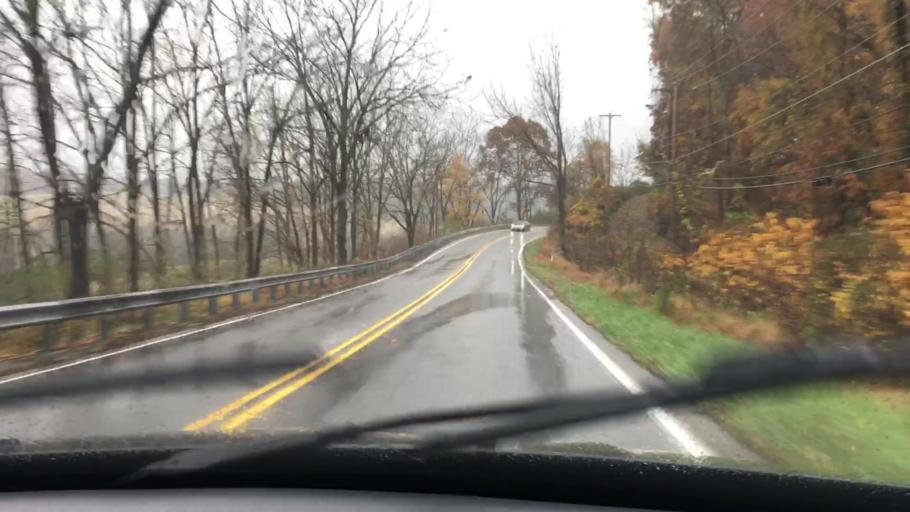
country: US
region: Pennsylvania
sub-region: York County
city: Glen Rock
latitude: 39.7727
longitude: -76.7315
